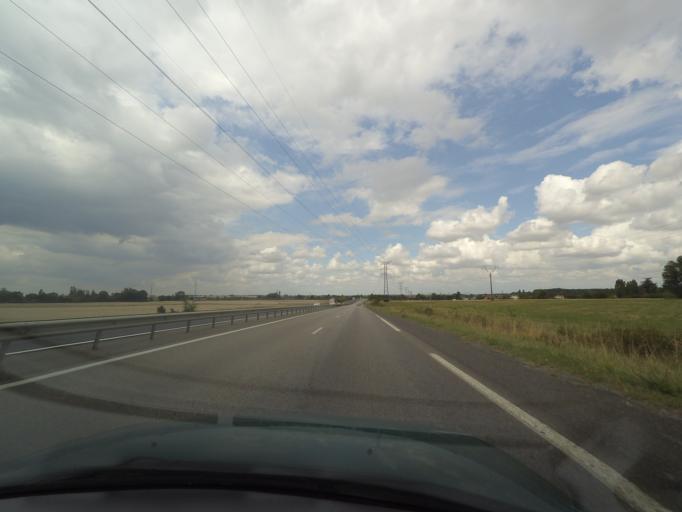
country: FR
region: Poitou-Charentes
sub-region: Departement de la Vienne
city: Mignaloux-Beauvoir
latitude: 46.5784
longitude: 0.3961
